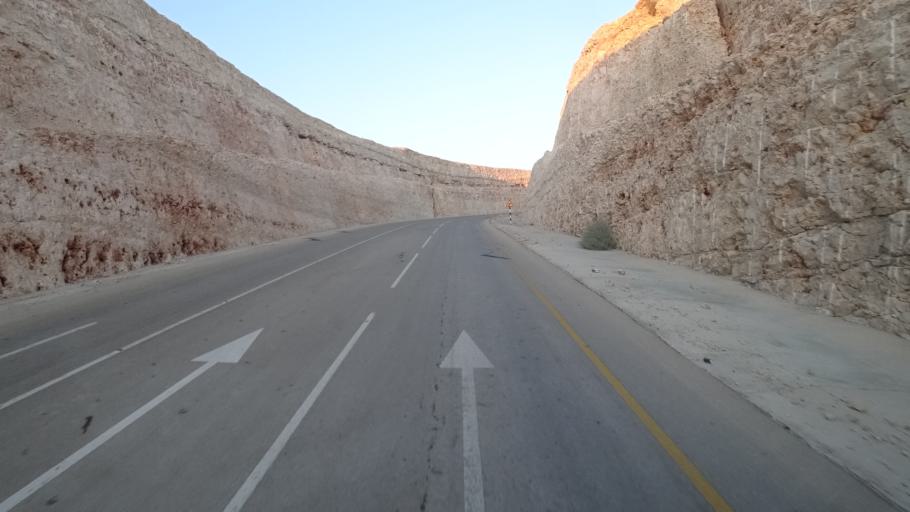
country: YE
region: Al Mahrah
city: Hawf
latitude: 16.9514
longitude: 53.3421
